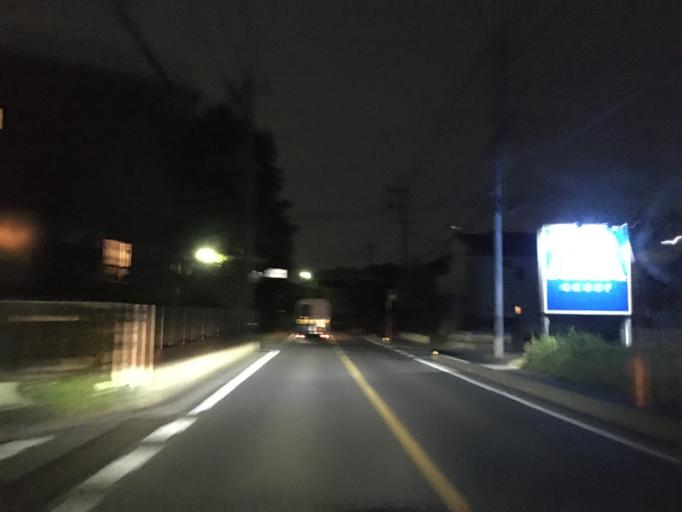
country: JP
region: Saitama
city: Sayama
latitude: 35.8804
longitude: 139.3871
